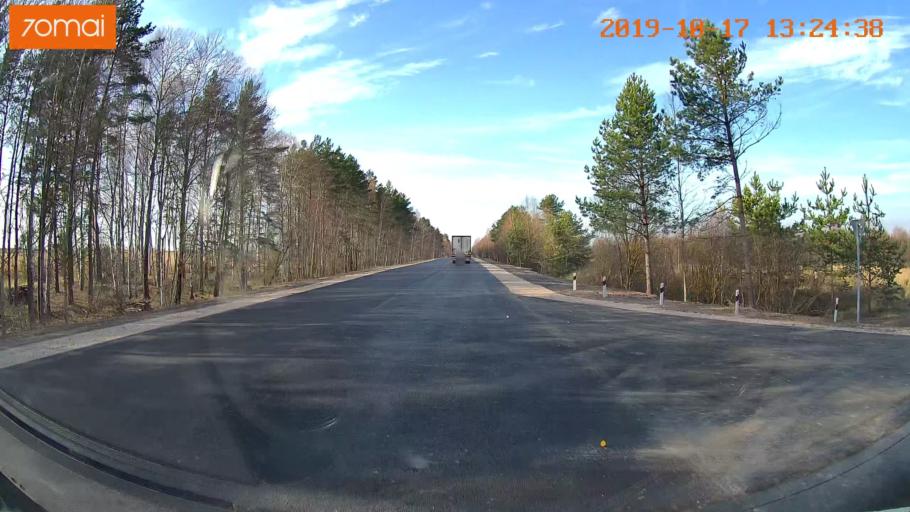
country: RU
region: Rjazan
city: Gus'-Zheleznyy
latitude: 55.0970
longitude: 40.9593
